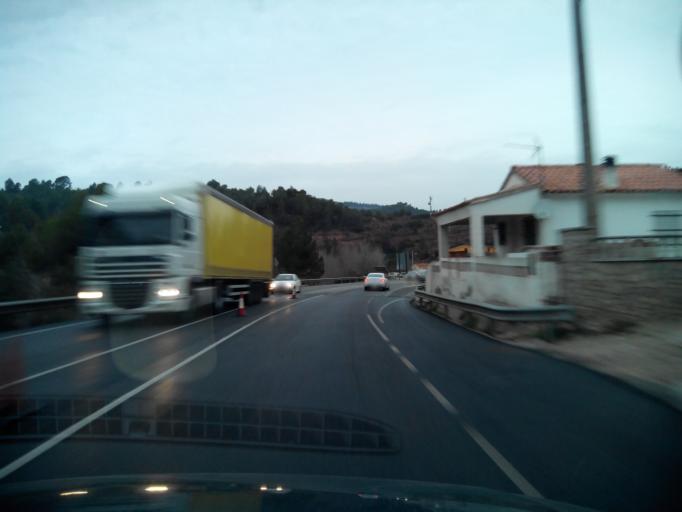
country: ES
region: Catalonia
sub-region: Provincia de Barcelona
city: Monistrol de Montserrat
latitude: 41.6168
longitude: 1.8680
